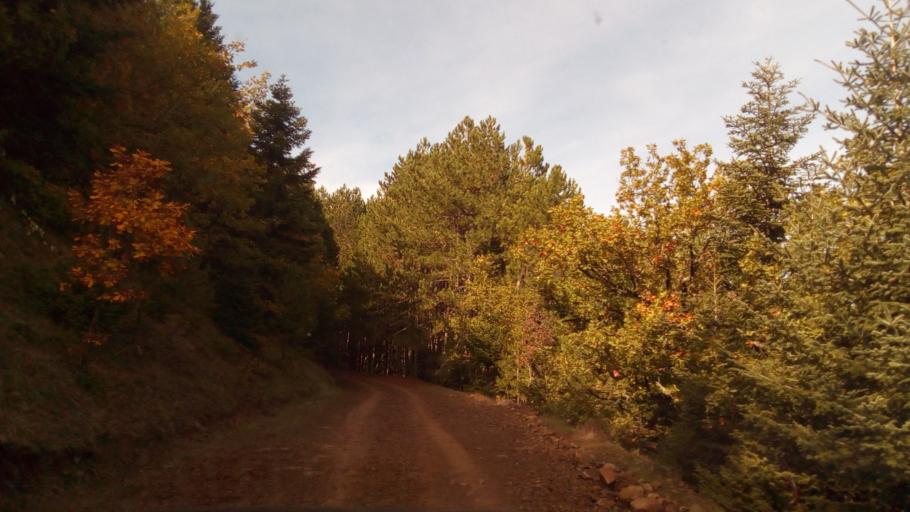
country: GR
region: Central Greece
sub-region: Nomos Fokidos
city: Lidoriki
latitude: 38.4804
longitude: 22.0521
